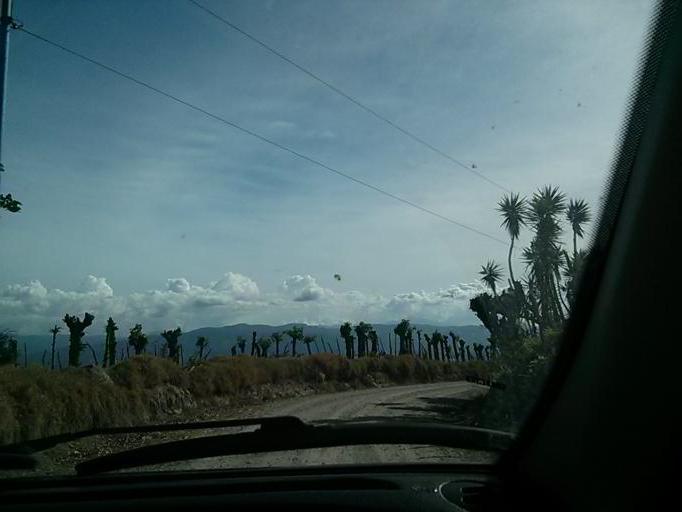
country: CR
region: Cartago
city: Cot
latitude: 9.9100
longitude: -83.9107
